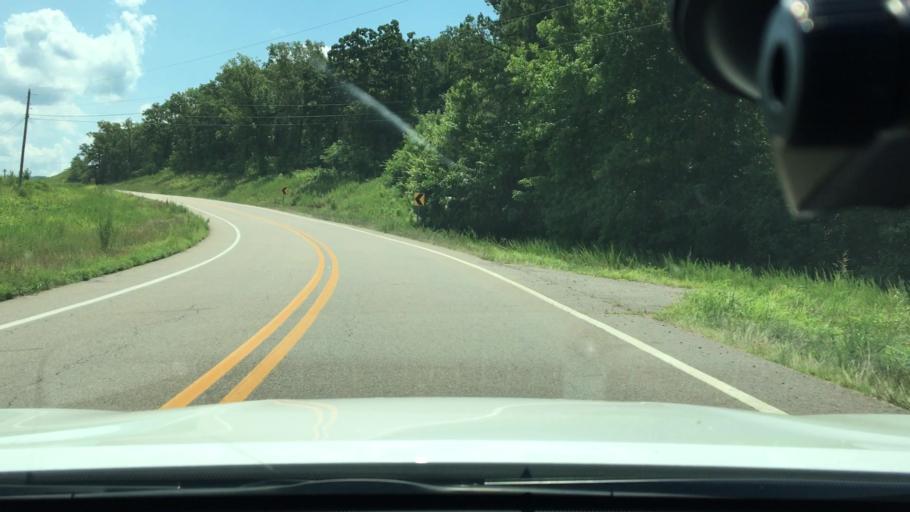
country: US
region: Arkansas
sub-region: Logan County
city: Paris
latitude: 35.2566
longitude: -93.6821
